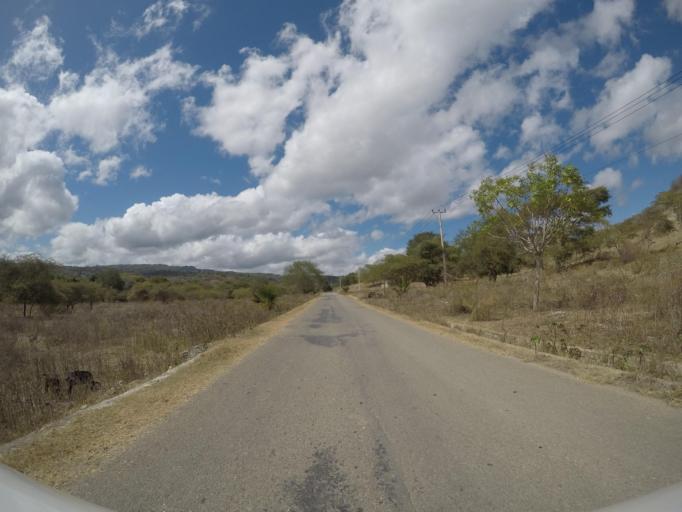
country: TL
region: Lautem
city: Lospalos
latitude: -8.4234
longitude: 126.8307
